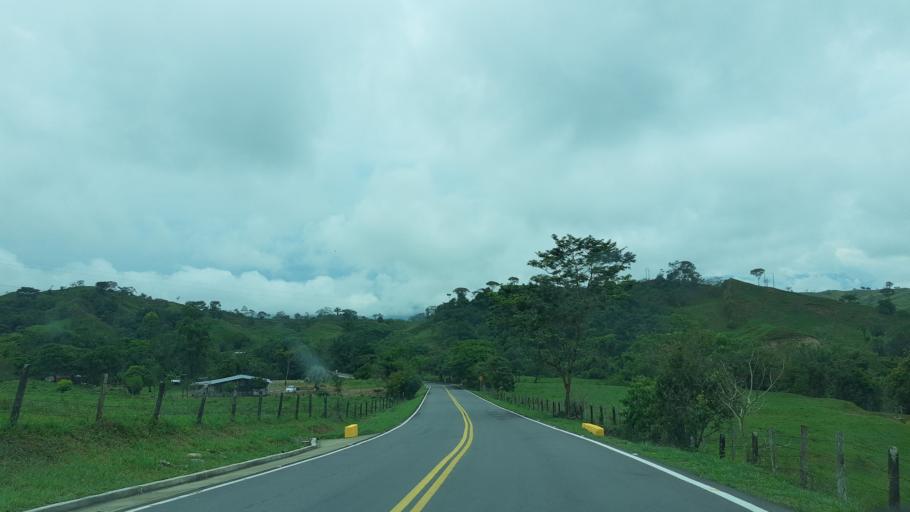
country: CO
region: Casanare
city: Sabanalarga
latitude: 4.7743
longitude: -73.0342
